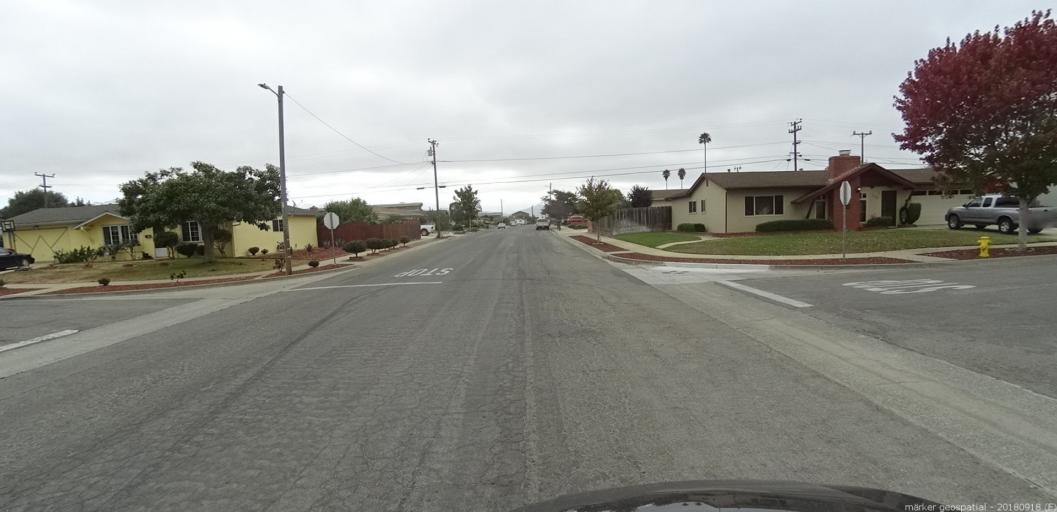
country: US
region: California
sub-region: Monterey County
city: Boronda
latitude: 36.7298
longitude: -121.6346
